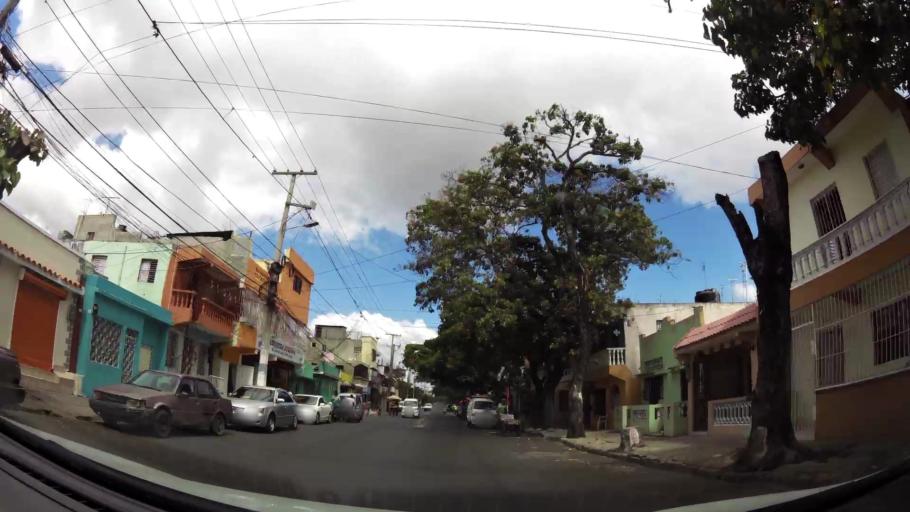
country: DO
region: Nacional
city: Ensanche Luperon
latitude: 18.4996
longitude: -69.8928
